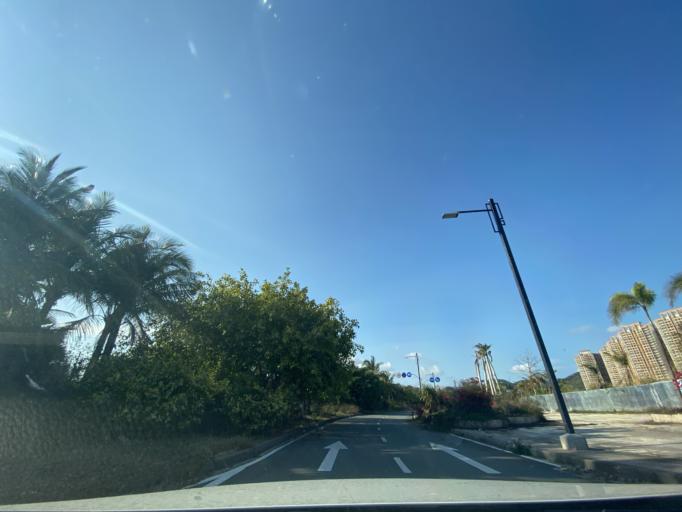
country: CN
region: Hainan
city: Yingzhou
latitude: 18.4535
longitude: 109.8553
